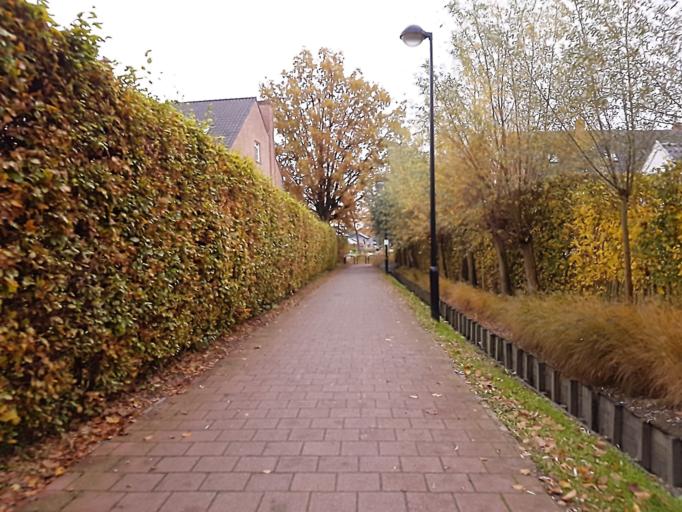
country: BE
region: Flanders
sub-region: Provincie Antwerpen
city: Hove
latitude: 51.1485
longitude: 4.4766
